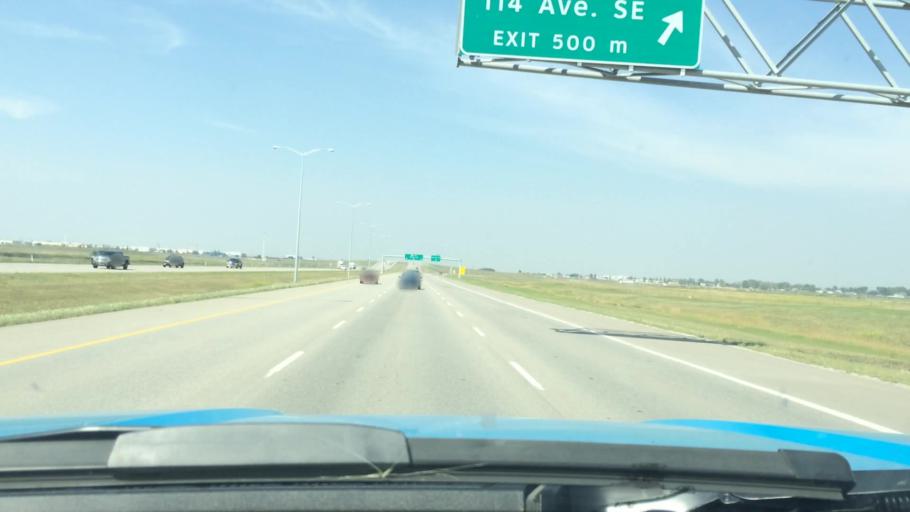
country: CA
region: Alberta
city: Chestermere
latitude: 50.9357
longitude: -113.9199
